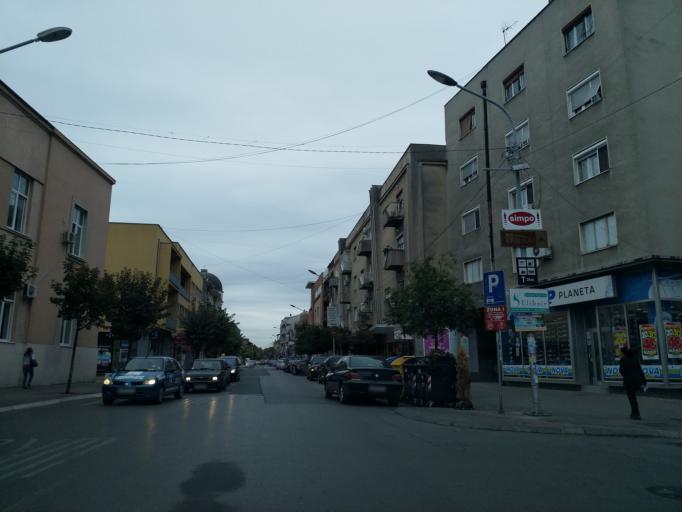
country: RS
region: Central Serbia
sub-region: Pomoravski Okrug
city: Jagodina
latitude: 43.9786
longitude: 21.2607
